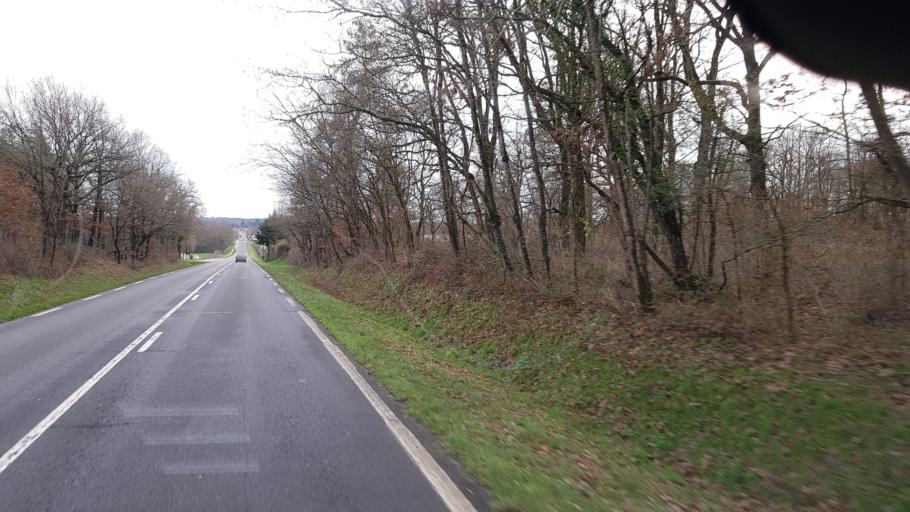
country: FR
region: Centre
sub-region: Departement du Loir-et-Cher
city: Lamotte-Beuvron
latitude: 47.6185
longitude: 2.0148
